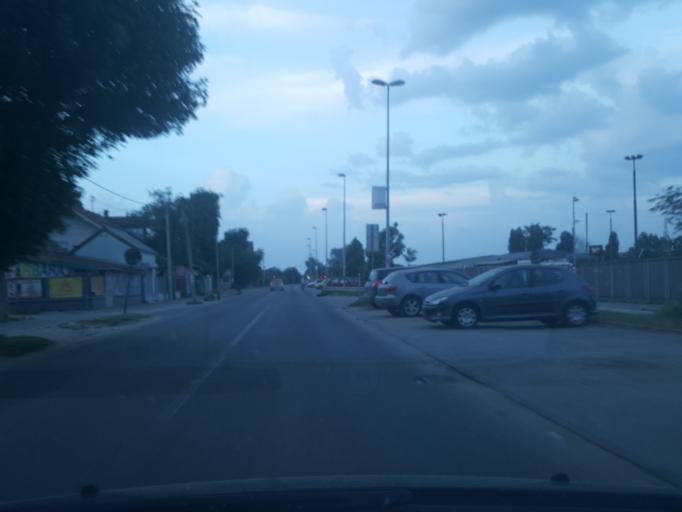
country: RS
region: Autonomna Pokrajina Vojvodina
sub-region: Juznobacki Okrug
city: Novi Sad
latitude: 45.2844
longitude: 19.8306
